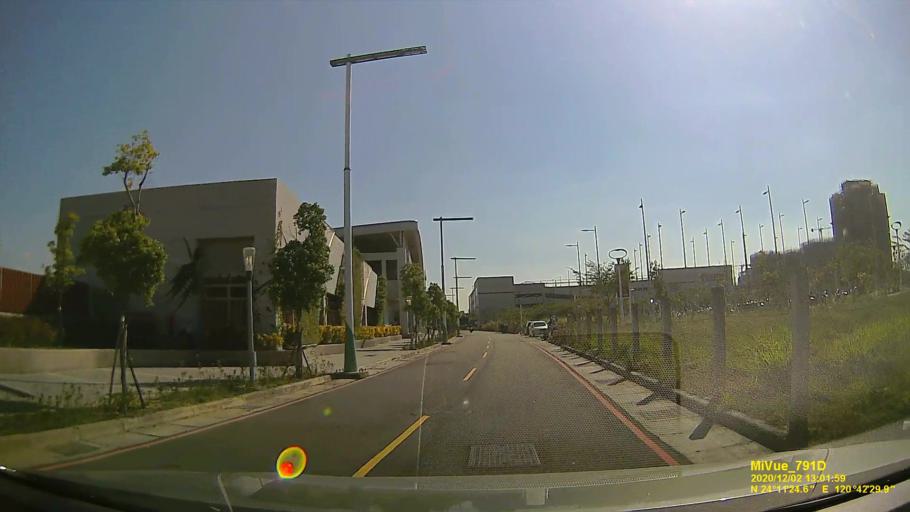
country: TW
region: Taiwan
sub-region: Taichung City
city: Taichung
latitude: 24.1902
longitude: 120.7081
